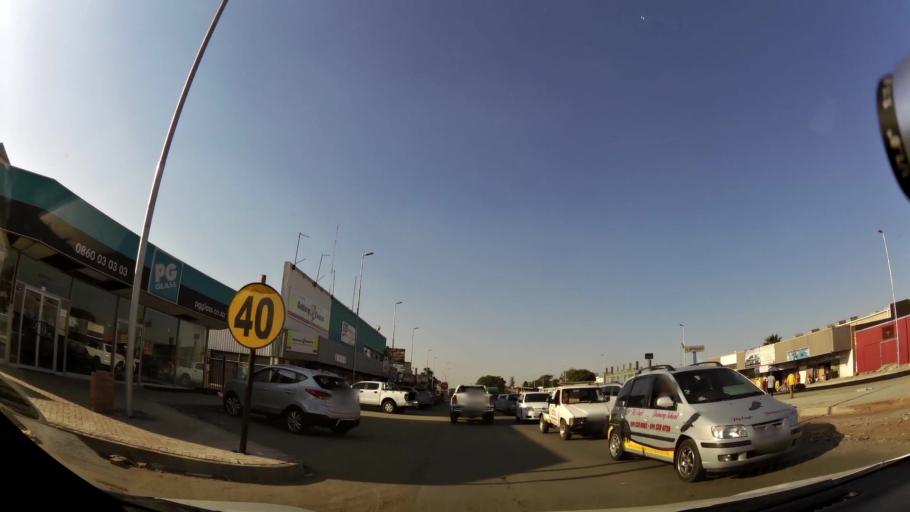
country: ZA
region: North-West
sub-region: Bojanala Platinum District Municipality
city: Rustenburg
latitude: -25.6648
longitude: 27.2430
